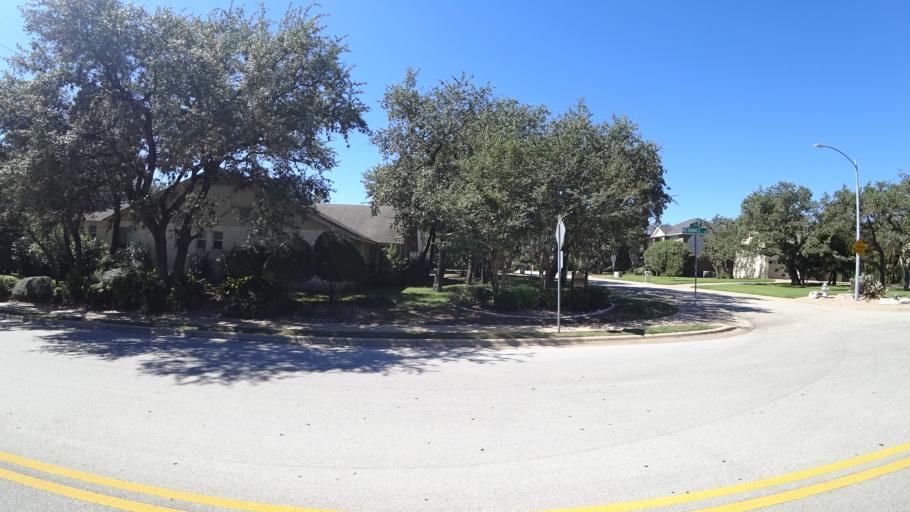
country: US
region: Texas
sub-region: Travis County
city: West Lake Hills
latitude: 30.3400
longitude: -97.7786
